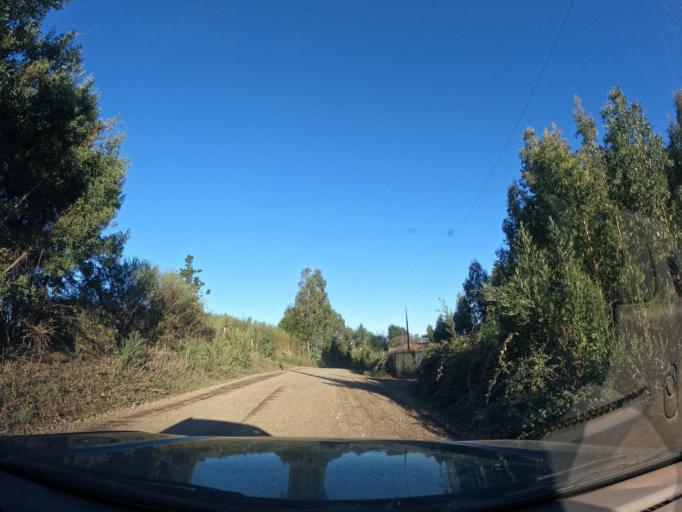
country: CL
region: Biobio
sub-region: Provincia de Concepcion
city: Chiguayante
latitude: -37.0309
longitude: -72.8707
